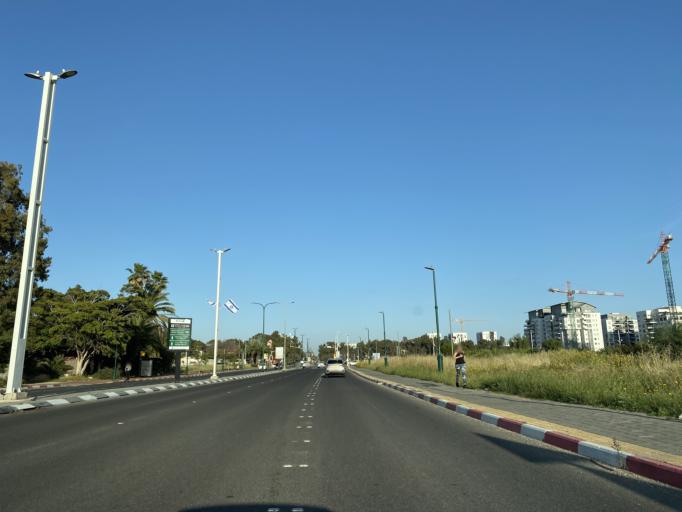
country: IL
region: Tel Aviv
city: Kefar Shemaryahu
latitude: 32.1786
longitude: 34.8284
